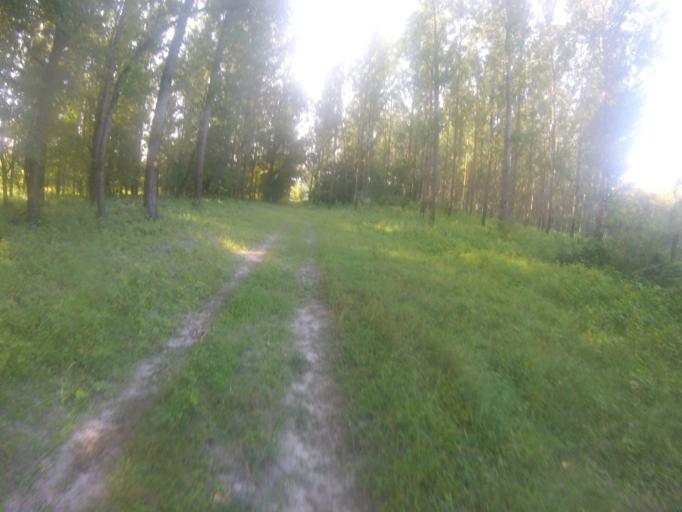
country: HU
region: Bacs-Kiskun
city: Baja
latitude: 46.1830
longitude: 18.9183
